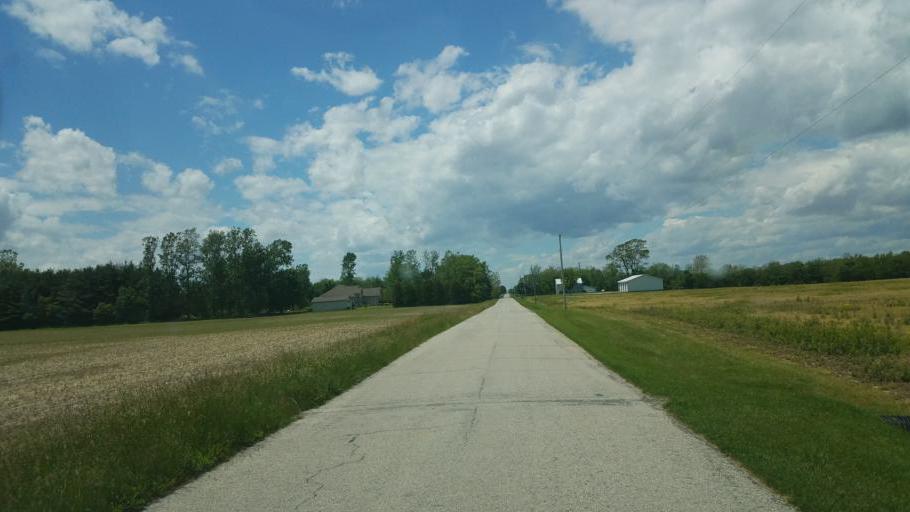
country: US
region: Ohio
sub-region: Huron County
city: Willard
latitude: 41.1428
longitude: -82.7766
